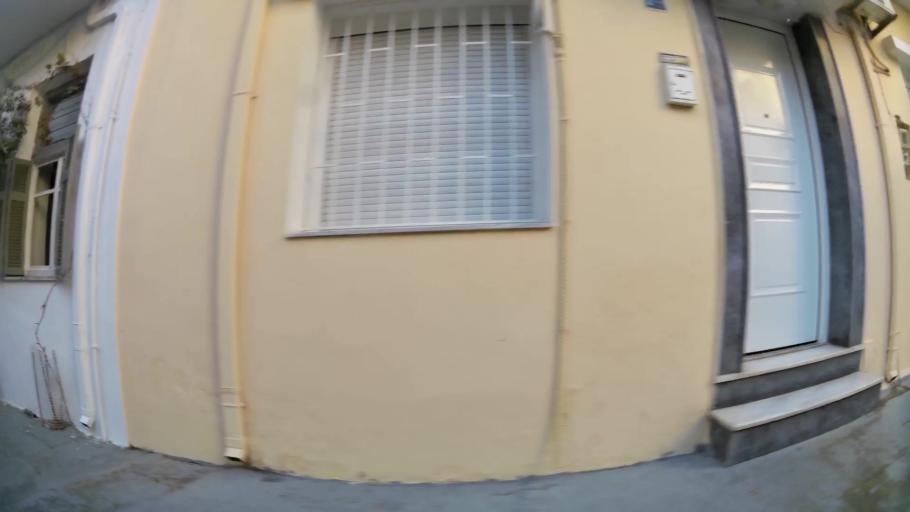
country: GR
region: Attica
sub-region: Nomos Piraios
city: Nikaia
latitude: 37.9628
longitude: 23.6390
